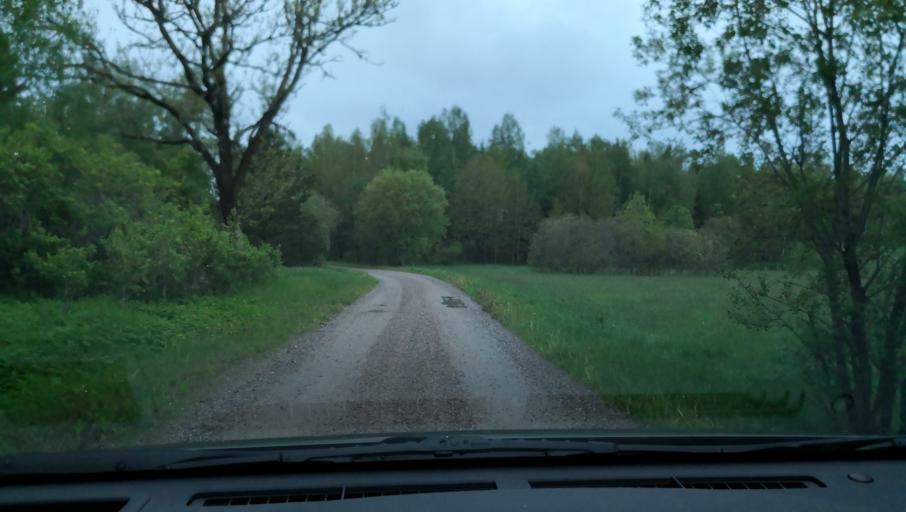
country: SE
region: Uppsala
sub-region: Heby Kommun
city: OEstervala
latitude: 59.9920
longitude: 17.2521
